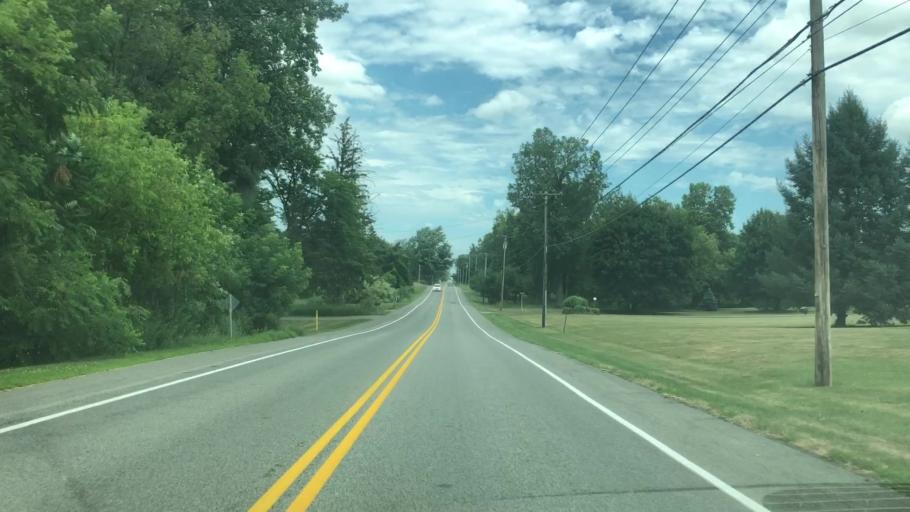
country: US
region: New York
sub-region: Monroe County
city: Fairport
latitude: 43.1343
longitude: -77.4005
